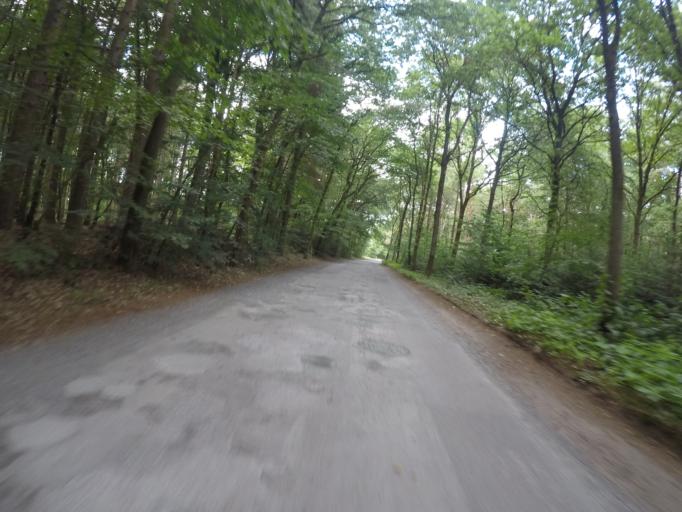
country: DE
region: Lower Saxony
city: Cadenberge
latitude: 53.7539
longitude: 9.0504
